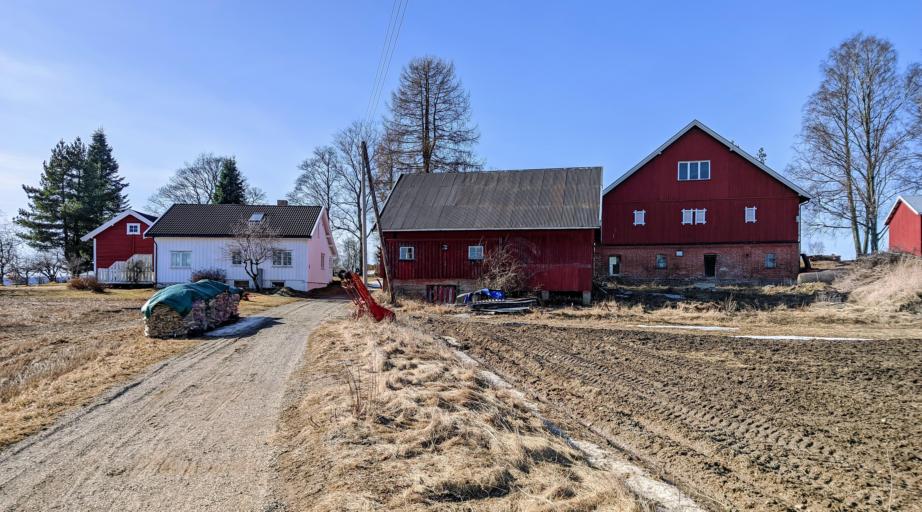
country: NO
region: Akershus
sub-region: Ullensaker
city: Jessheim
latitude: 60.1468
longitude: 11.1433
